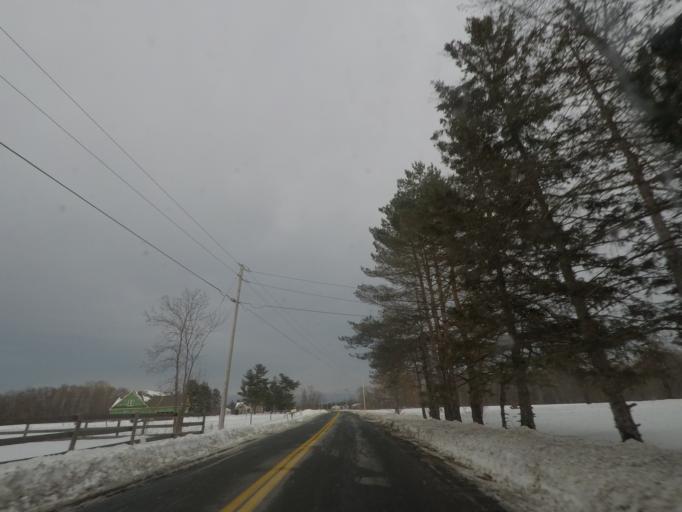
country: US
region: New York
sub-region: Rensselaer County
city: Castleton-on-Hudson
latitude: 42.5170
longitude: -73.7464
